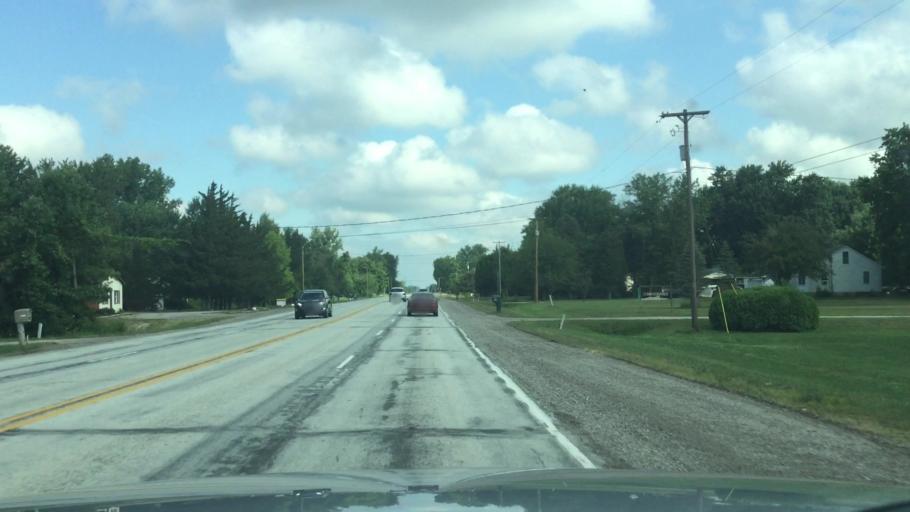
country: US
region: Michigan
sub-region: Genesee County
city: Clio
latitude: 43.2247
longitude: -83.7501
